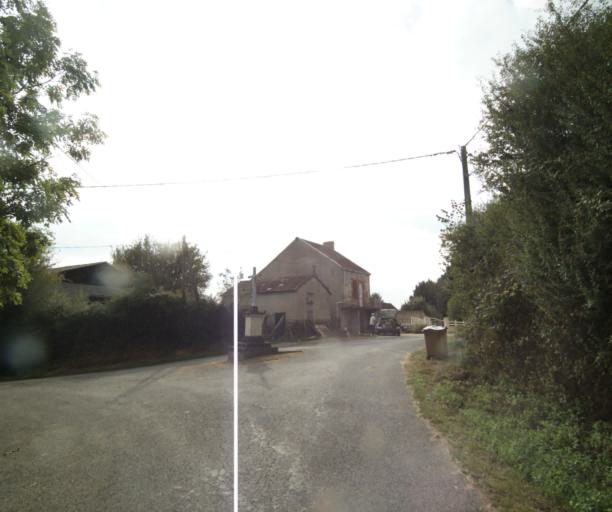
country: FR
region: Bourgogne
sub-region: Departement de Saone-et-Loire
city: Palinges
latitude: 46.5250
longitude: 4.2636
